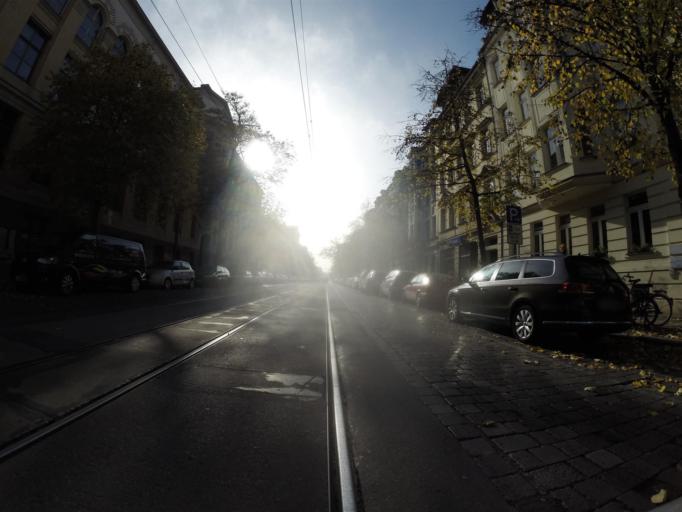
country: DE
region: Saxony
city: Leipzig
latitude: 51.3259
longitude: 12.3449
